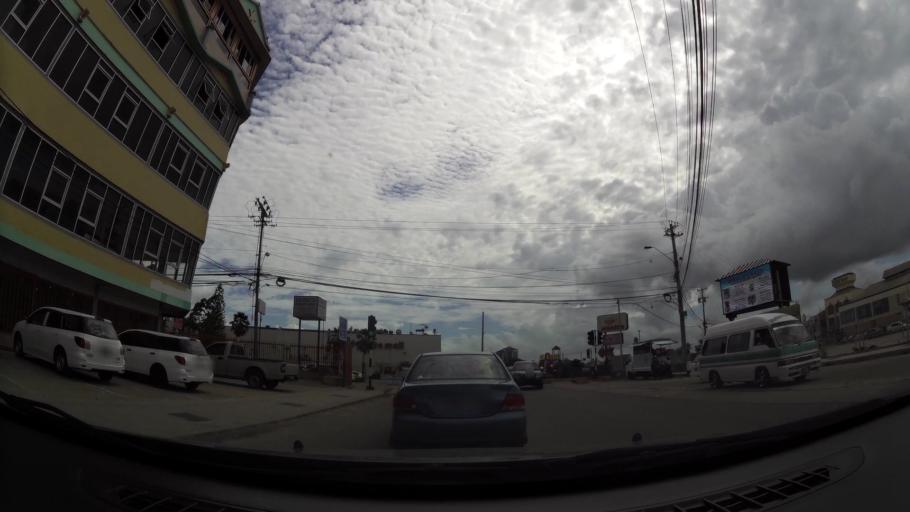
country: TT
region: Chaguanas
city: Chaguanas
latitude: 10.5125
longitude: -61.4096
